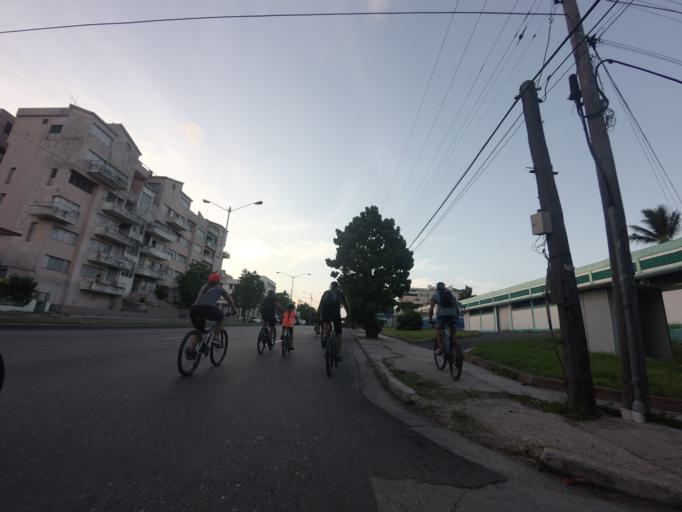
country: CU
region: La Habana
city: Havana
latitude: 23.1181
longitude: -82.4017
